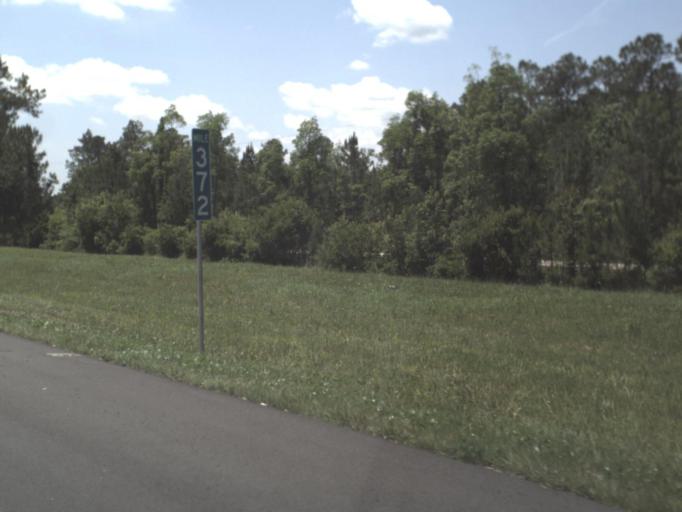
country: US
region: Florida
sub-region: Nassau County
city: Yulee
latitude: 30.6088
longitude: -81.6464
